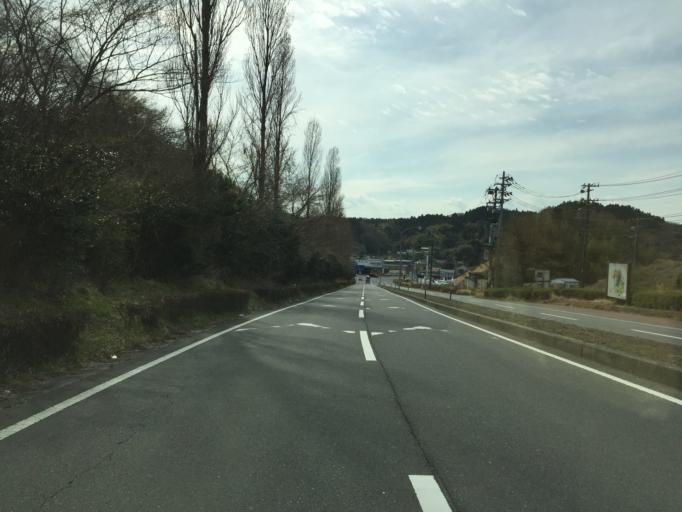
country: JP
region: Fukushima
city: Iwaki
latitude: 37.0067
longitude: 140.9114
